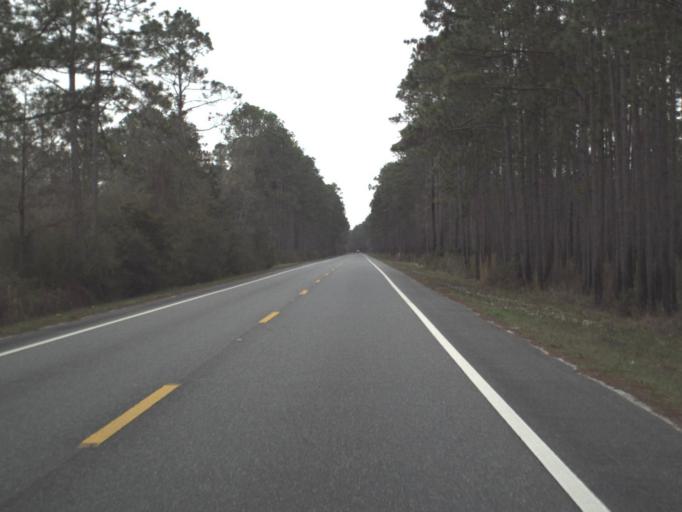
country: US
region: Florida
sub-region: Franklin County
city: Apalachicola
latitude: 29.9700
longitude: -84.9754
